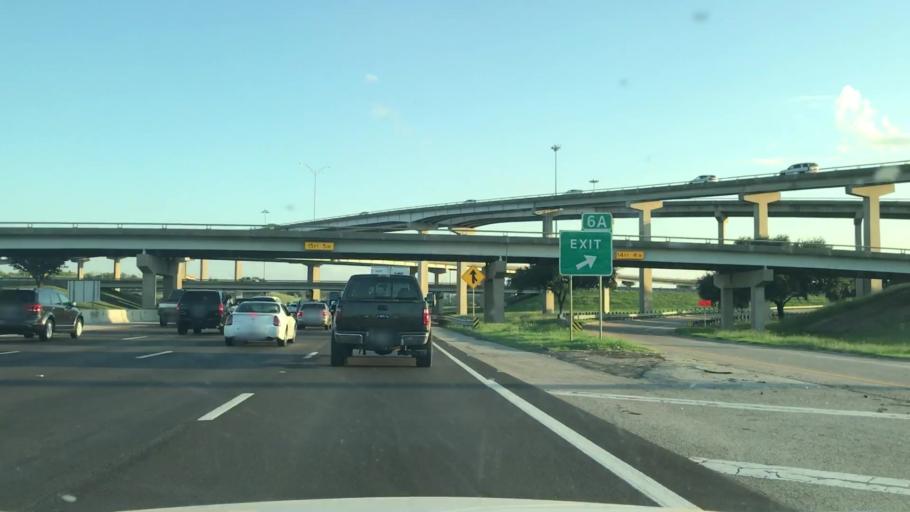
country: US
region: Texas
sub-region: Dallas County
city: Mesquite
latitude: 32.7945
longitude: -96.6256
